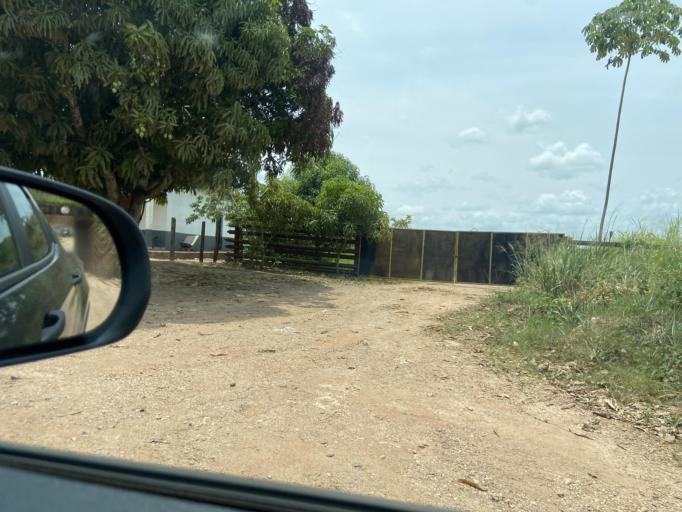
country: BR
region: Para
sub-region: Maraba
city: Maraba
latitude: -5.3278
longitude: -49.0858
